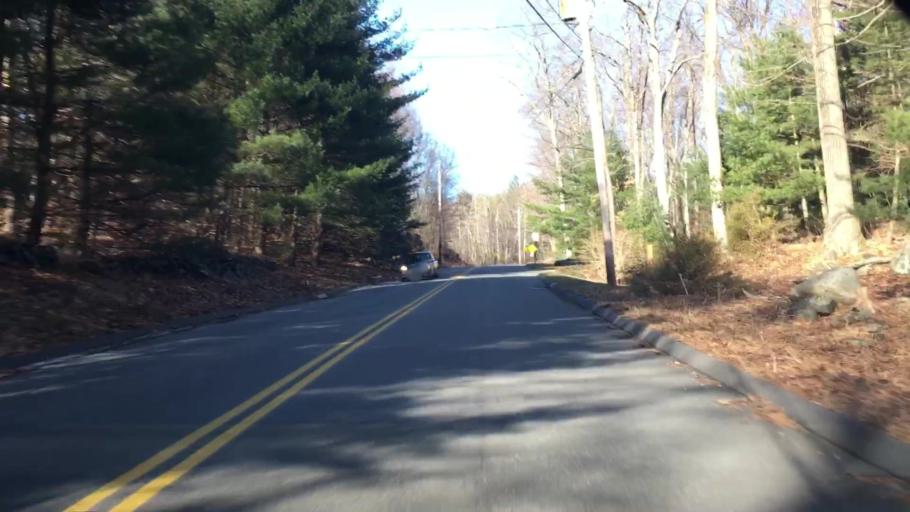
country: US
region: Connecticut
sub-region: Tolland County
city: Tolland
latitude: 41.8801
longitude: -72.3816
